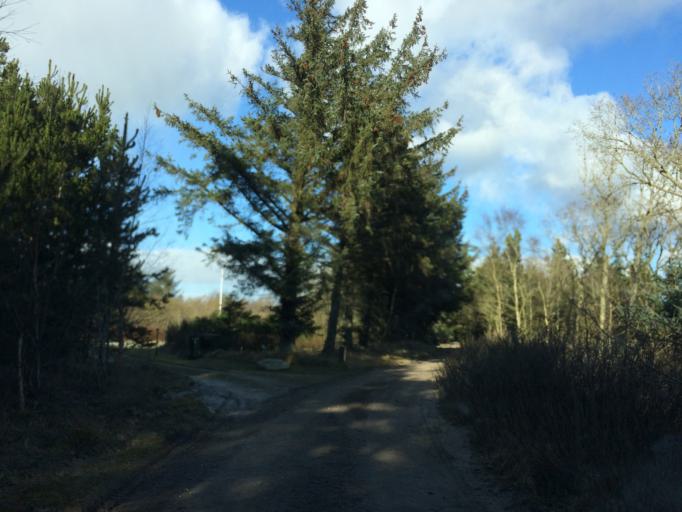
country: DK
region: Central Jutland
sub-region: Holstebro Kommune
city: Ulfborg
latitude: 56.2617
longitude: 8.1434
